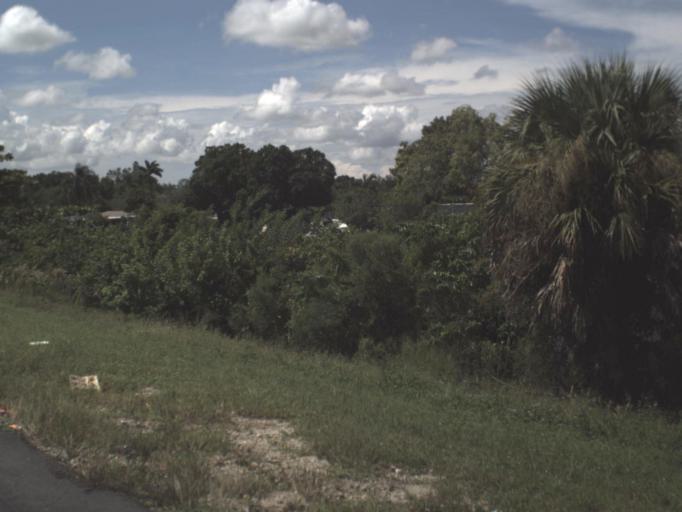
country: US
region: Florida
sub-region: Lee County
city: Tice
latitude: 26.6909
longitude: -81.7990
